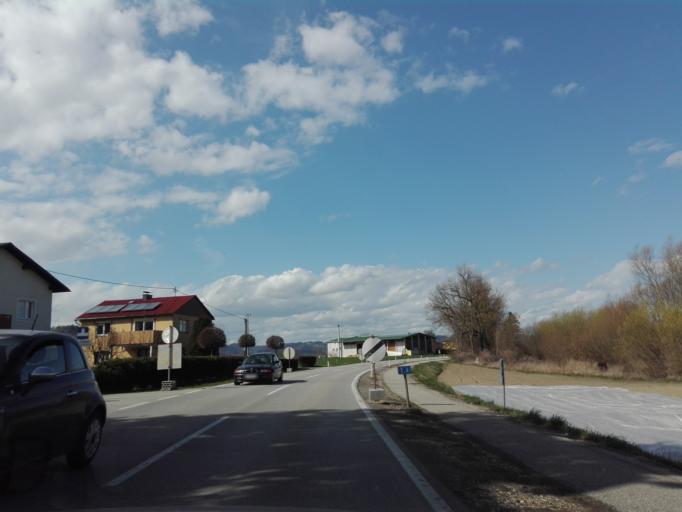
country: AT
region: Upper Austria
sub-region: Politischer Bezirk Urfahr-Umgebung
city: Feldkirchen an der Donau
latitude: 48.3185
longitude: 14.0128
